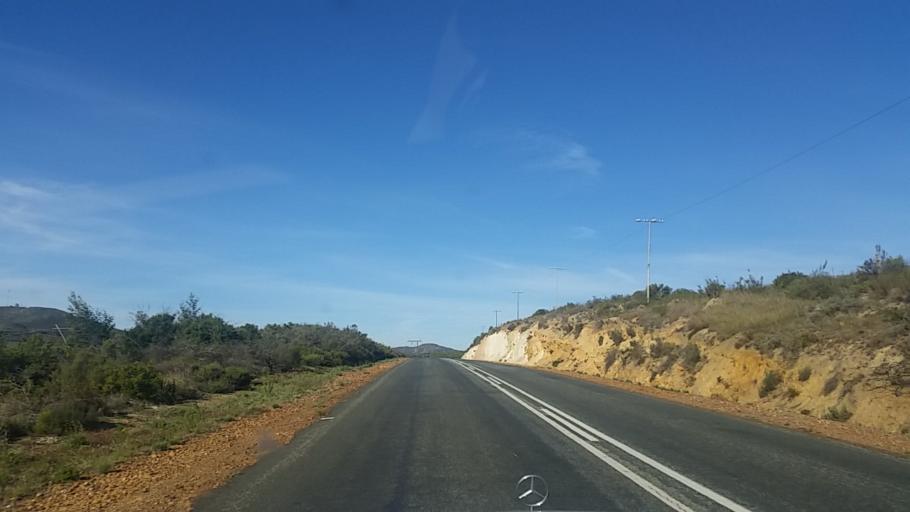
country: ZA
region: Western Cape
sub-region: Eden District Municipality
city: Knysna
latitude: -33.7419
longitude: 23.0324
